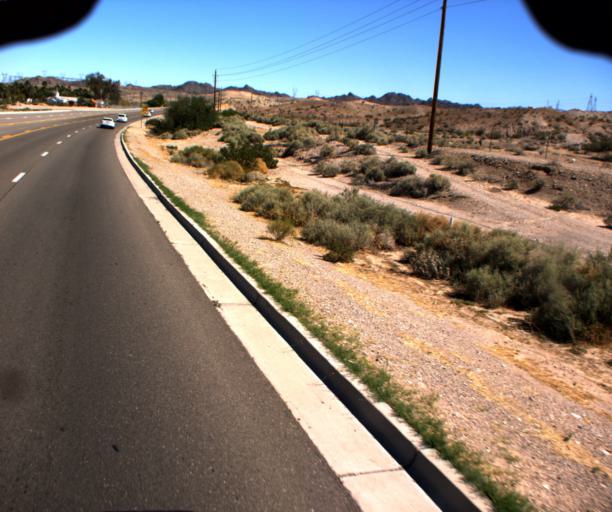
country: US
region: Nevada
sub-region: Clark County
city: Laughlin
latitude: 35.1746
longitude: -114.5656
